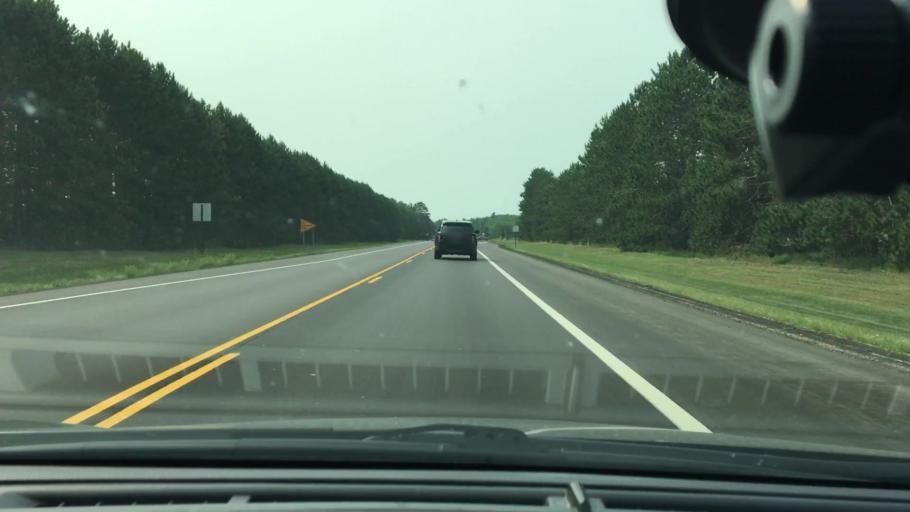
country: US
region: Minnesota
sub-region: Crow Wing County
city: Brainerd
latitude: 46.4309
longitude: -94.1747
